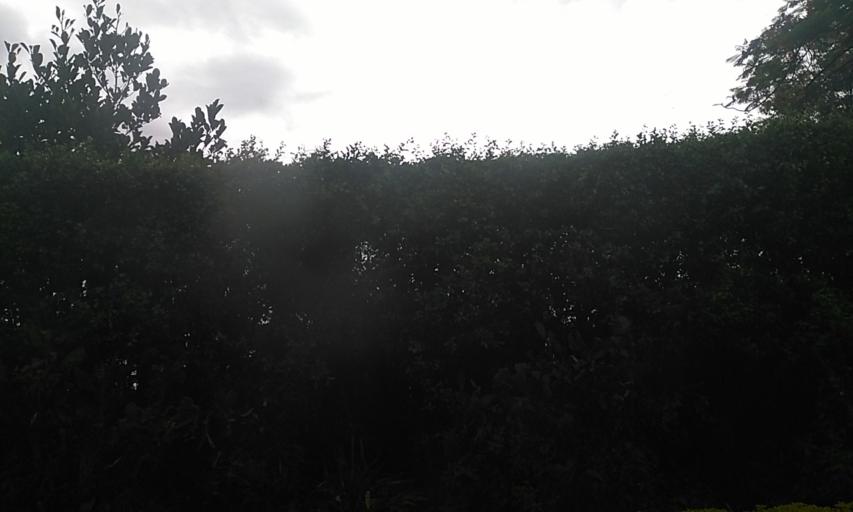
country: UG
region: Central Region
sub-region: Kampala District
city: Kampala
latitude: 0.3281
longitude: 32.5955
